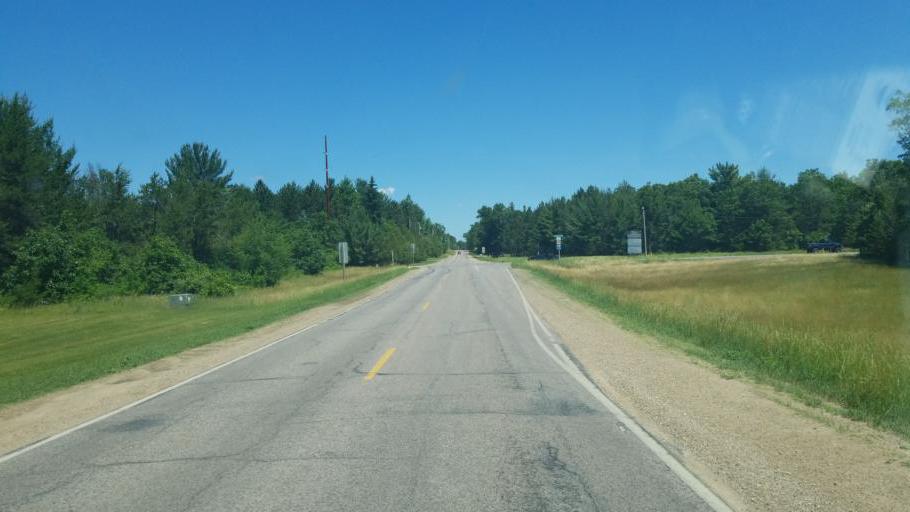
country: US
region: Wisconsin
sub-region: Adams County
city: Adams
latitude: 43.9726
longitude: -89.9379
